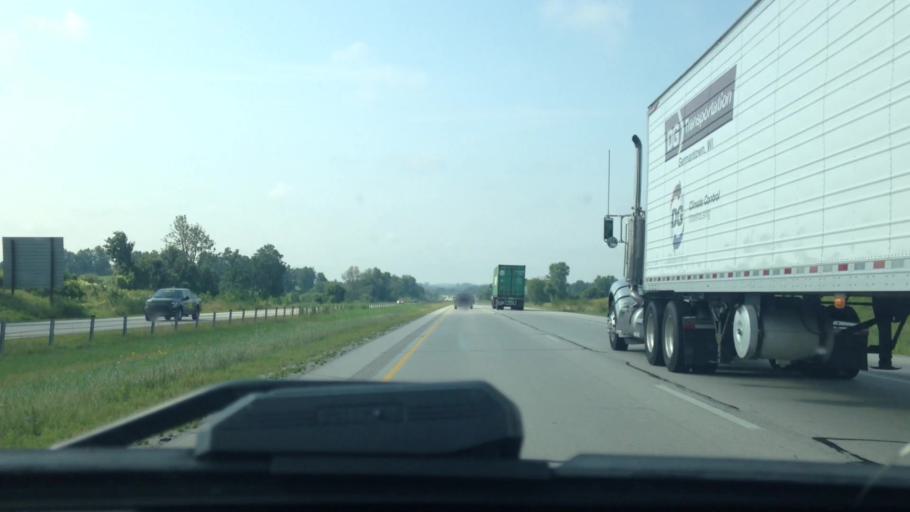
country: US
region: Wisconsin
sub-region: Dodge County
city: Lomira
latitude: 43.5779
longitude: -88.4307
